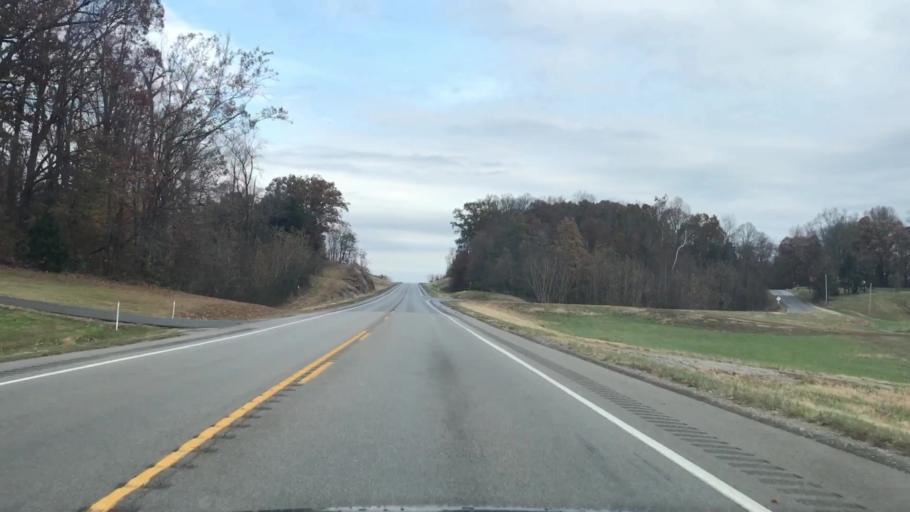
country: US
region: Kentucky
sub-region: Monroe County
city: Tompkinsville
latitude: 36.7616
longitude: -85.6861
